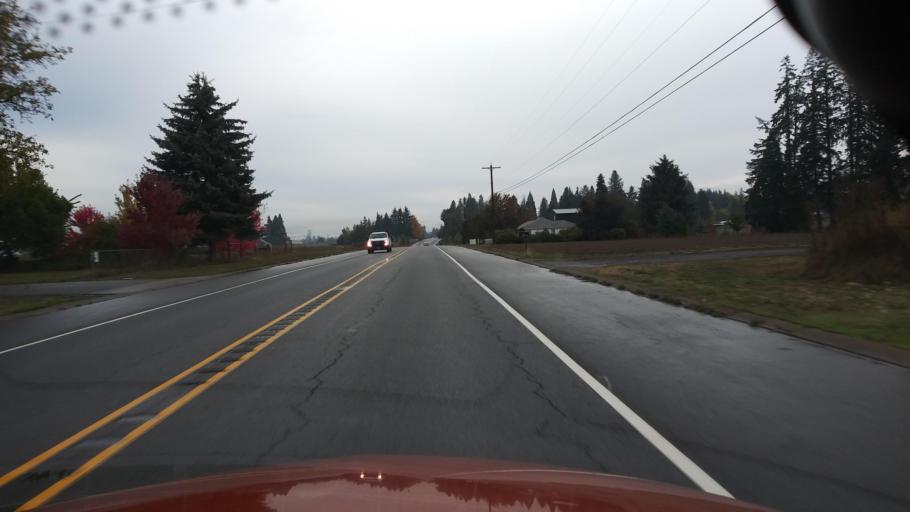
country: US
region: Oregon
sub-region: Washington County
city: Cornelius
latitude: 45.5352
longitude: -123.0598
